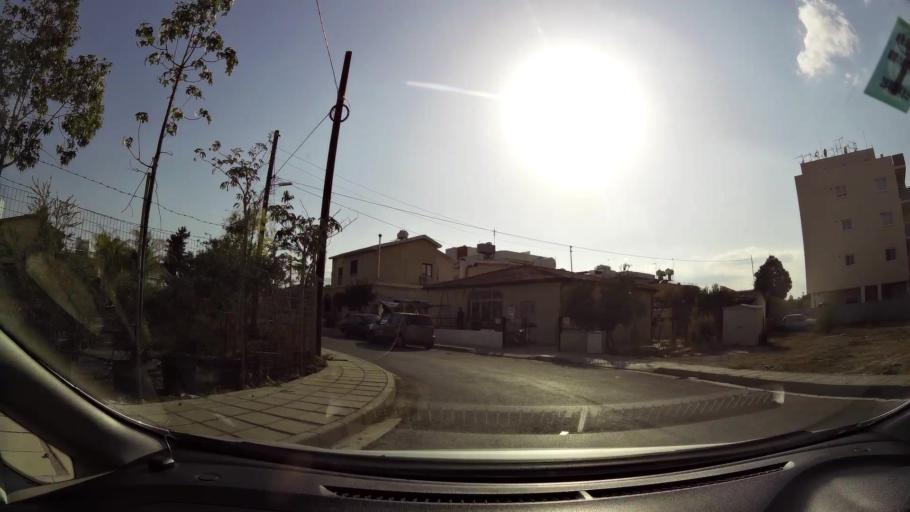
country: CY
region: Lefkosia
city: Nicosia
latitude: 35.1792
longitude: 33.3334
